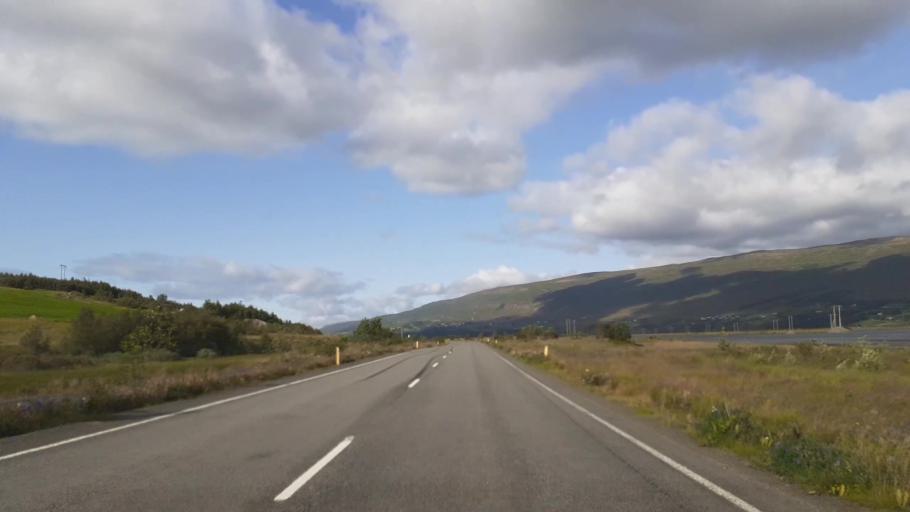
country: IS
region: Northeast
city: Akureyri
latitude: 65.6273
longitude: -18.0718
